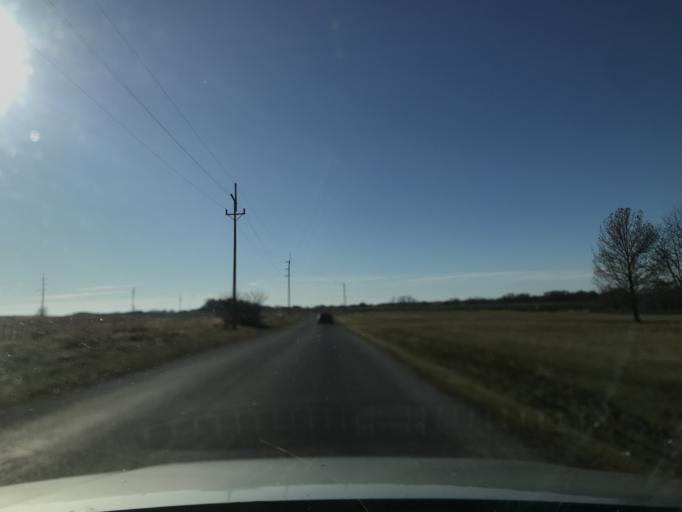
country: US
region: Illinois
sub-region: Hancock County
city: Carthage
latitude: 40.4629
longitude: -91.1784
